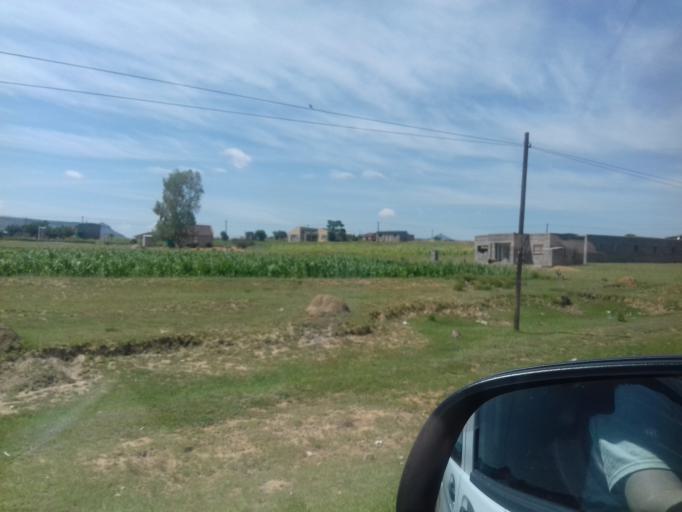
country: LS
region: Mafeteng
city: Mafeteng
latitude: -29.7045
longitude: 27.4284
